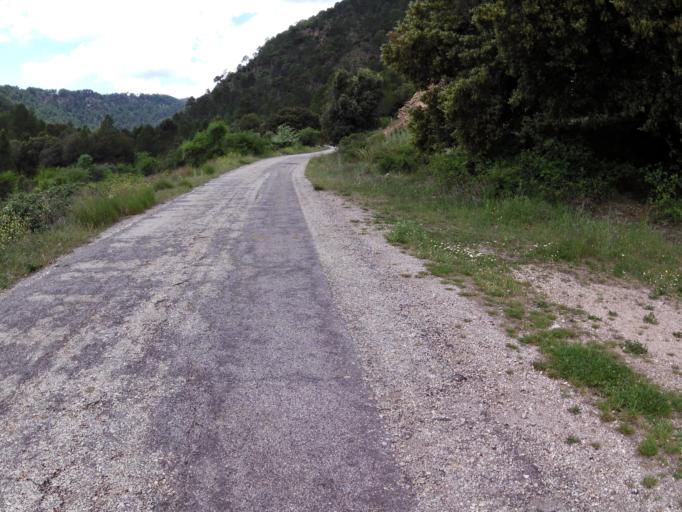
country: ES
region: Castille-La Mancha
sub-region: Provincia de Albacete
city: Paterna del Madera
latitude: 38.5786
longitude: -2.3505
